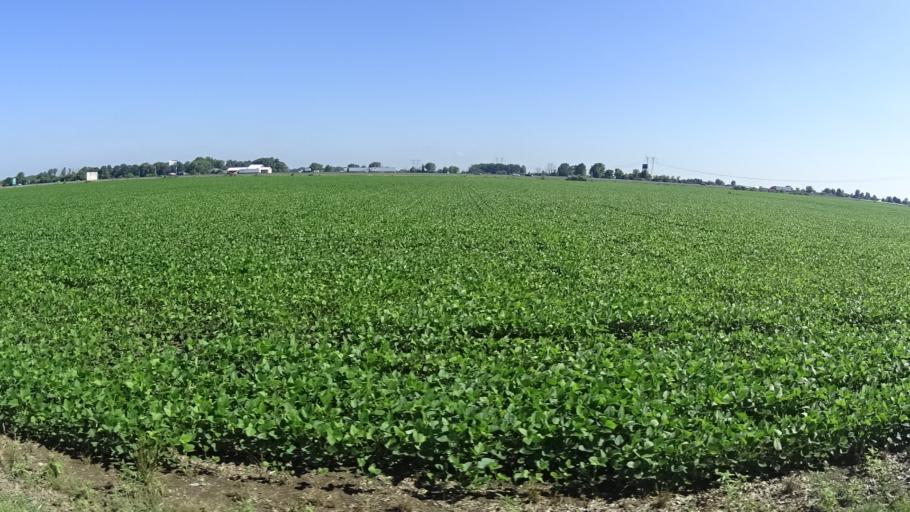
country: US
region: Indiana
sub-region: Madison County
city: Ingalls
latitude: 39.9878
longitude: -85.8212
